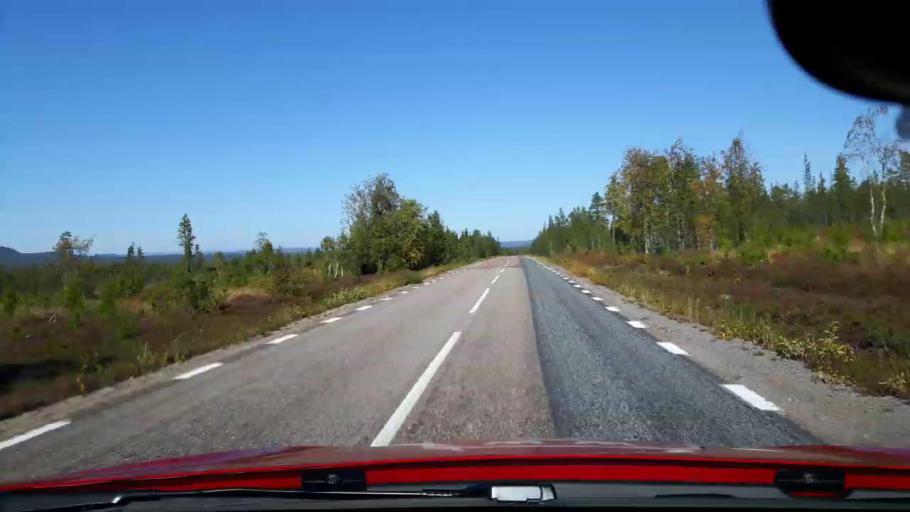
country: SE
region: Jaemtland
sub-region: Harjedalens Kommun
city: Sveg
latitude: 61.7293
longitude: 14.1654
